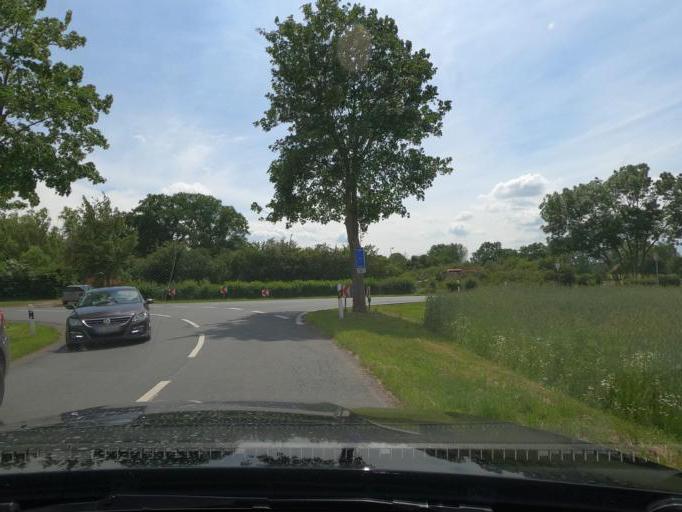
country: DE
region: Lower Saxony
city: Schwarmstedt
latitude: 52.6380
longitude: 9.6051
